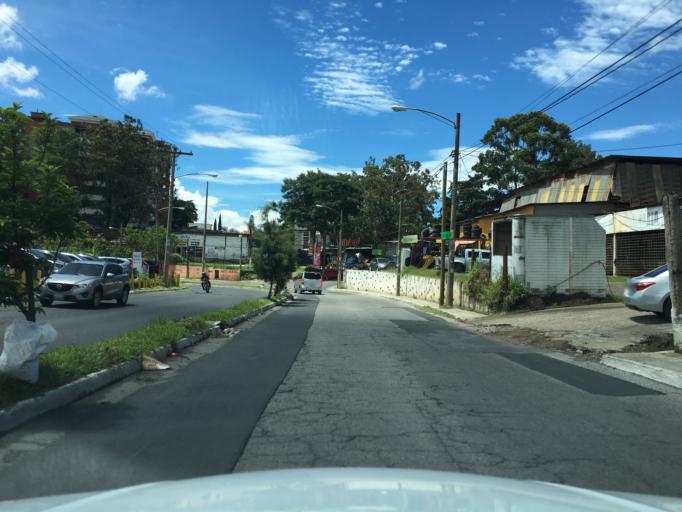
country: GT
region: Guatemala
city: Guatemala City
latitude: 14.6431
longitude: -90.5570
